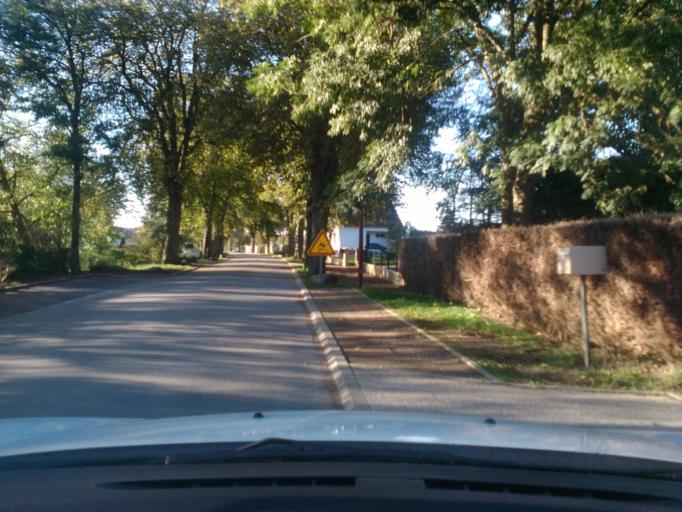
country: FR
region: Lorraine
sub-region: Departement des Vosges
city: Rambervillers
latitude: 48.2958
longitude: 6.6040
